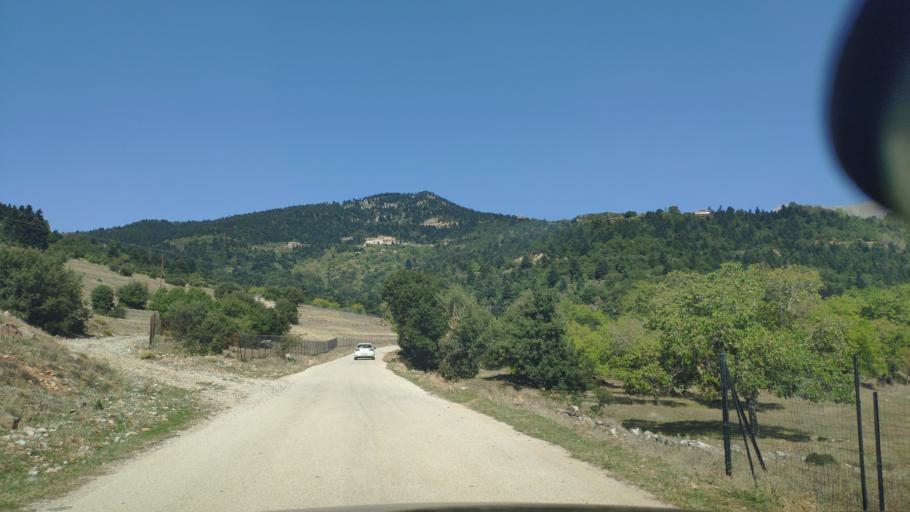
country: GR
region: Peloponnese
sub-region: Nomos Korinthias
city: Nemea
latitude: 37.8549
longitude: 22.3851
